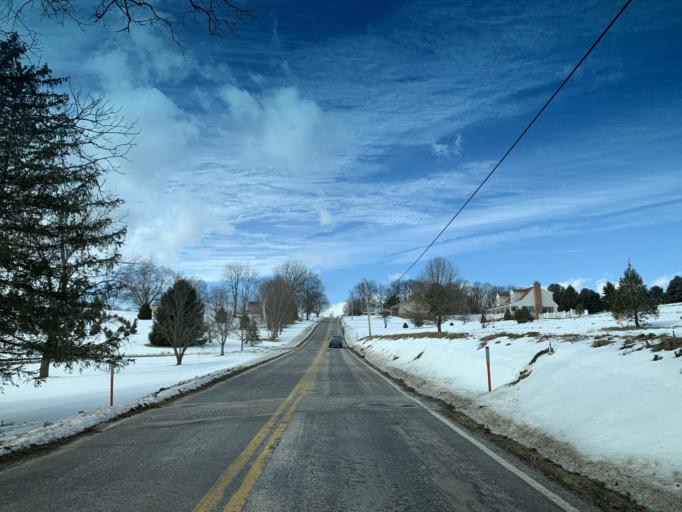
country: US
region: Pennsylvania
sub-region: York County
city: Shrewsbury
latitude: 39.8039
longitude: -76.6623
